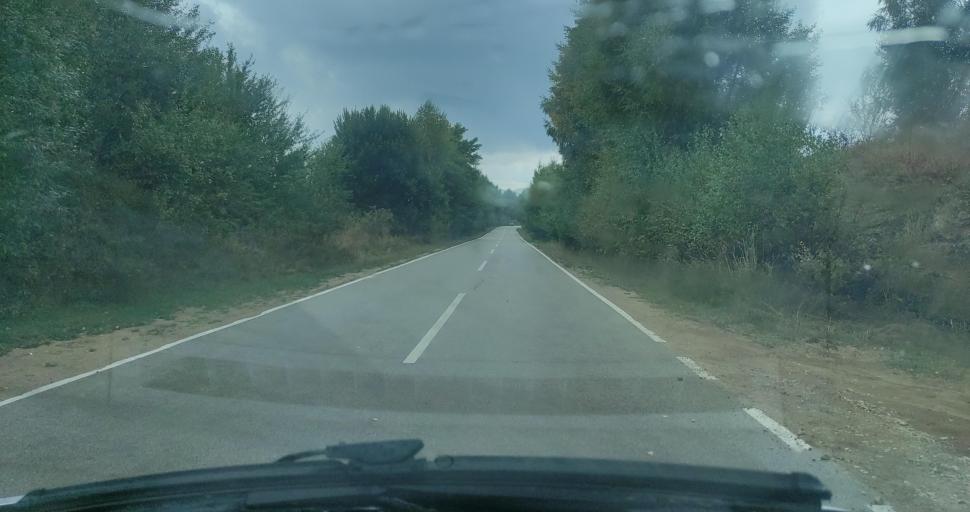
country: RS
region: Central Serbia
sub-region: Jablanicki Okrug
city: Crna Trava
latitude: 42.7102
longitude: 22.3277
